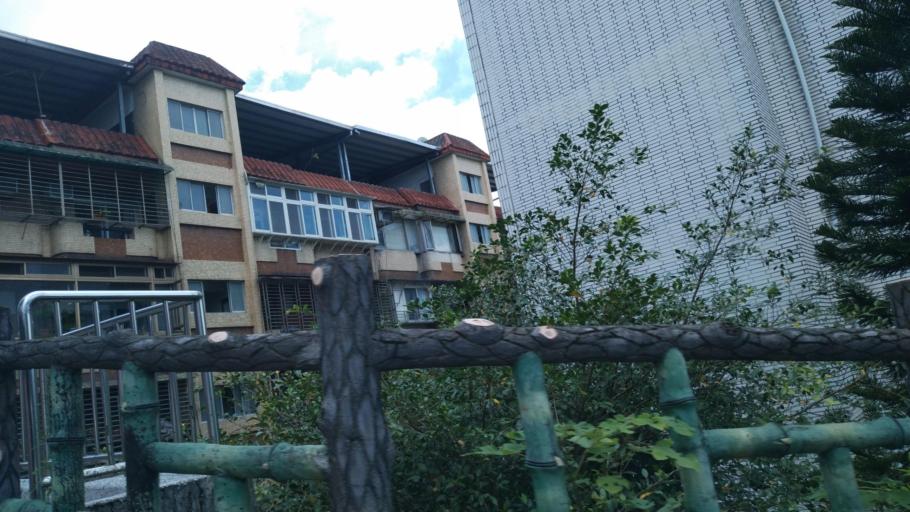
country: TW
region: Taipei
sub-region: Taipei
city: Banqiao
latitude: 24.9490
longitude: 121.4963
